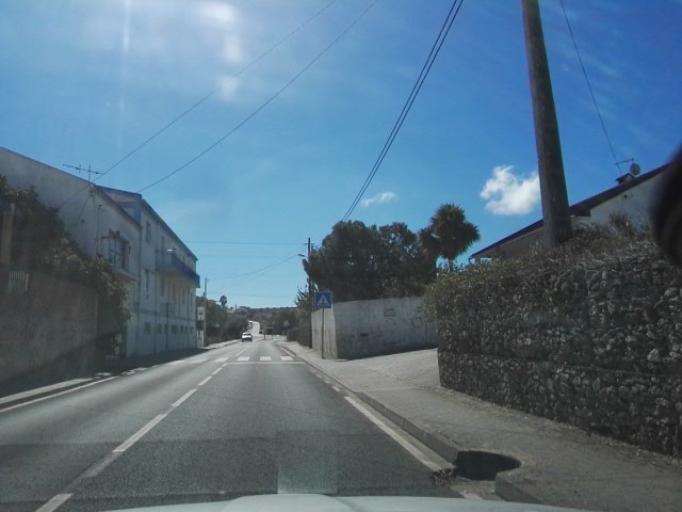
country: PT
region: Lisbon
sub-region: Arruda Dos Vinhos
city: Arruda dos Vinhos
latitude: 38.9606
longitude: -9.0598
